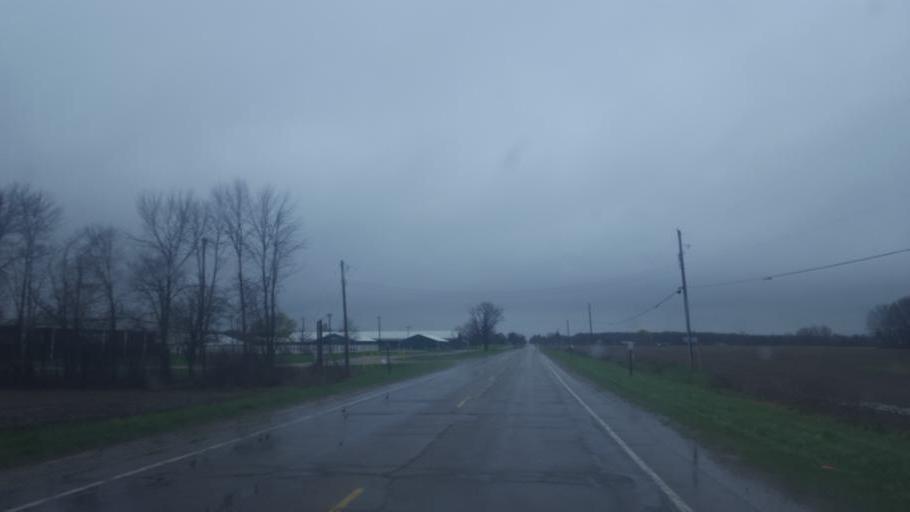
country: US
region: Michigan
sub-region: Isabella County
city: Mount Pleasant
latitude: 43.6501
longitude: -84.7682
